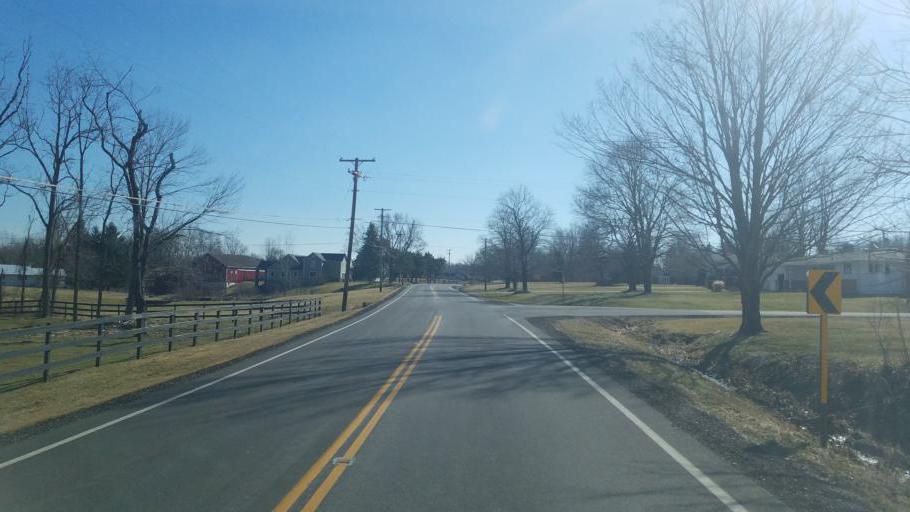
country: US
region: Ohio
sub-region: Richland County
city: Ontario
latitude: 40.7479
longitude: -82.6620
